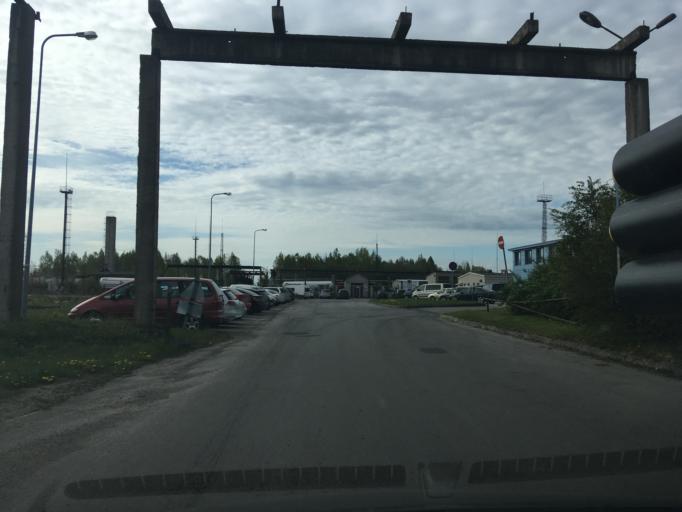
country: EE
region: Harju
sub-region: Tallinna linn
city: Kose
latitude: 59.4272
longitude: 24.8549
